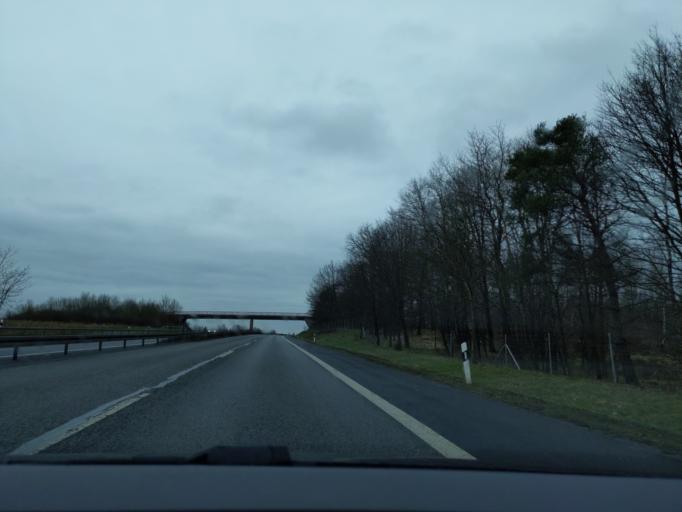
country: DE
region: Hesse
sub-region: Regierungsbezirk Giessen
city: Fronhausen
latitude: 50.7135
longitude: 8.7278
